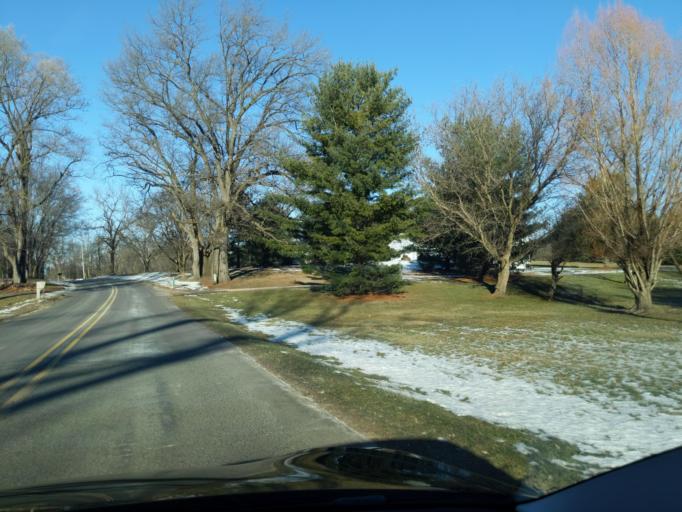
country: US
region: Michigan
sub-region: Ingham County
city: Stockbridge
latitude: 42.4320
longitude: -84.1508
